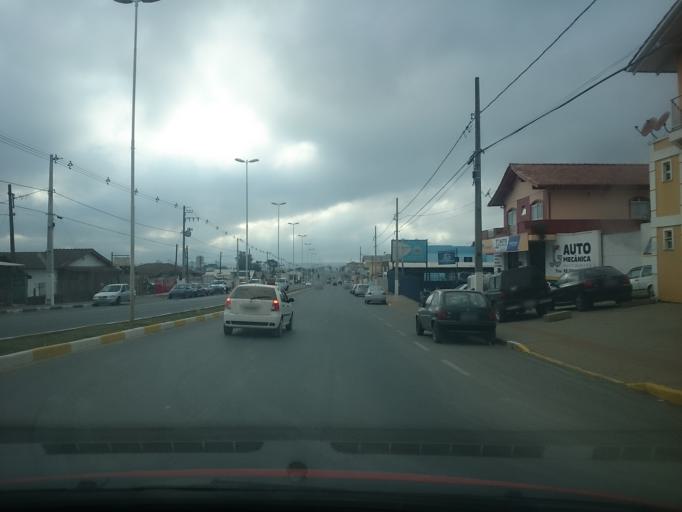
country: BR
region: Santa Catarina
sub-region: Lages
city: Lages
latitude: -27.8321
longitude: -50.3462
